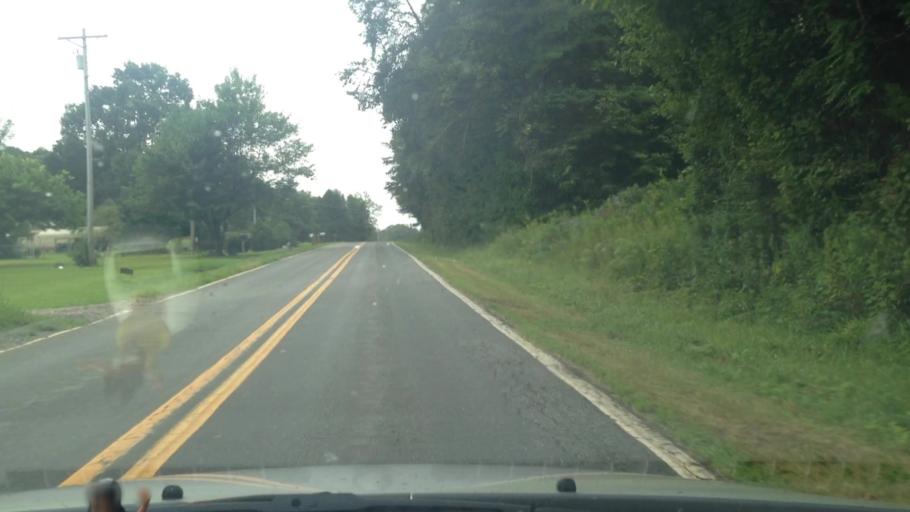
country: US
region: North Carolina
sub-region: Stokes County
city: Danbury
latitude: 36.3876
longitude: -80.1356
